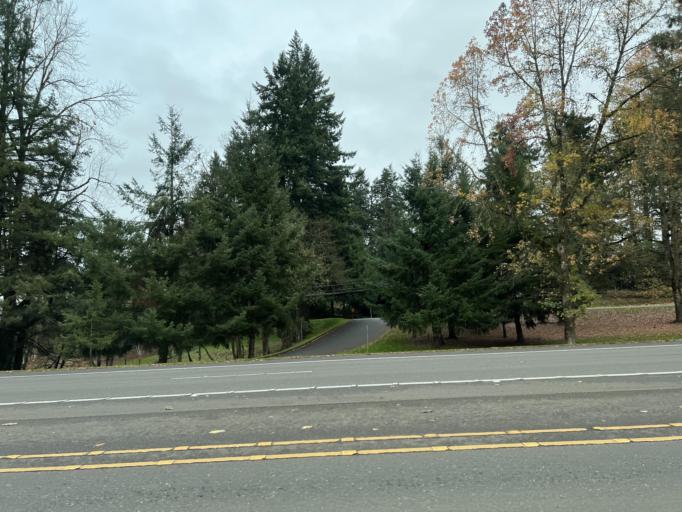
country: US
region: Oregon
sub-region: Marion County
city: Salem
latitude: 44.8953
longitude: -123.0369
